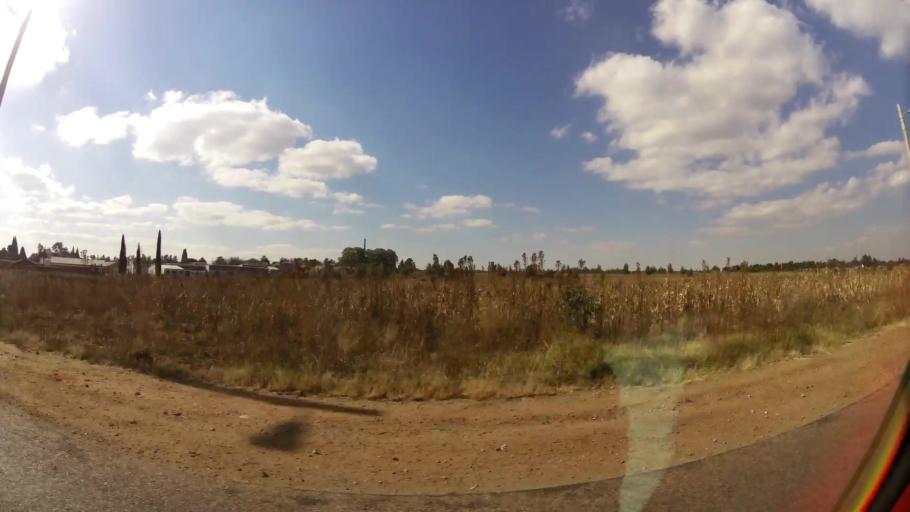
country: ZA
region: Gauteng
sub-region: Ekurhuleni Metropolitan Municipality
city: Tembisa
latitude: -25.9830
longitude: 28.2462
